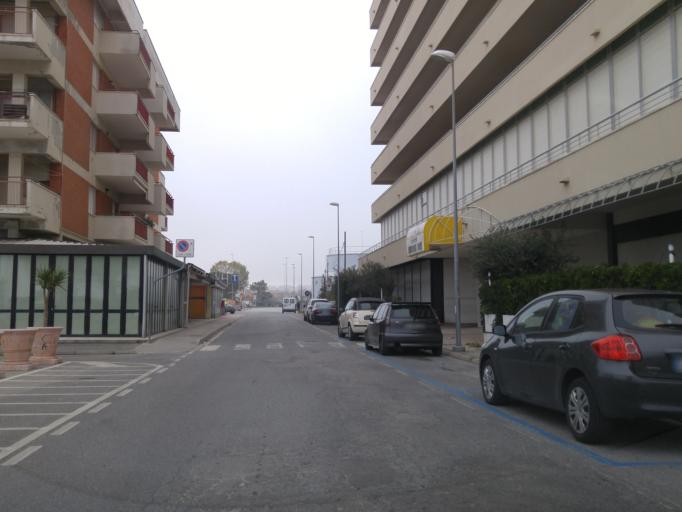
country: IT
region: Emilia-Romagna
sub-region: Provincia di Rimini
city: Montalbano
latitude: 43.9700
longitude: 12.7240
